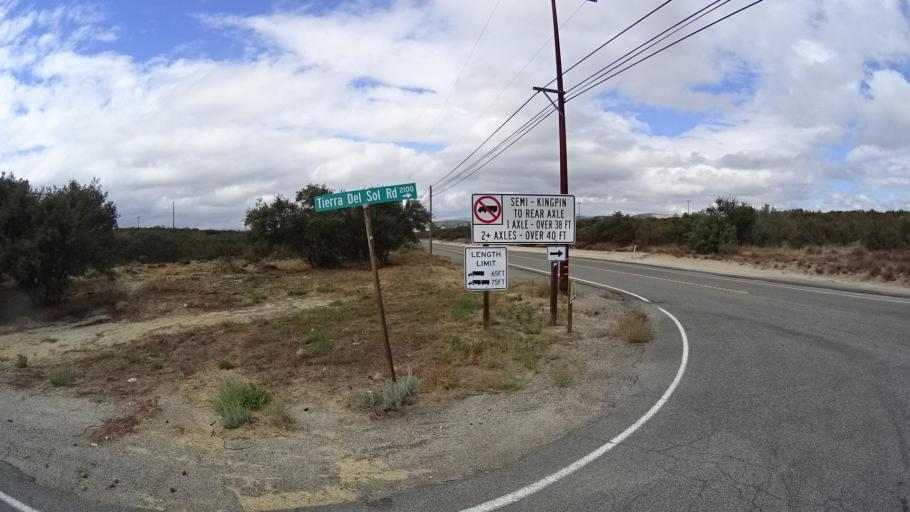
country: US
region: California
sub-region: San Diego County
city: Campo
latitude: 32.6656
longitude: -116.3167
